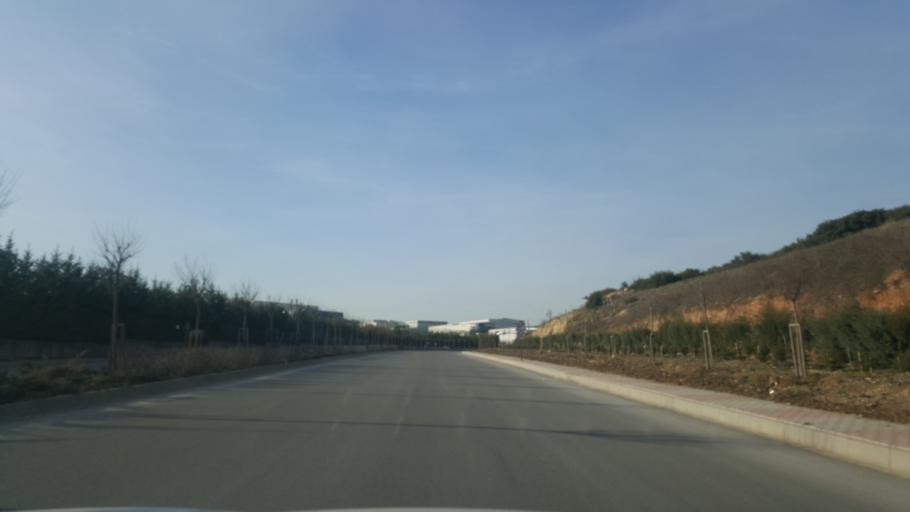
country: TR
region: Kocaeli
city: Tavsancil
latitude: 40.8138
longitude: 29.5669
